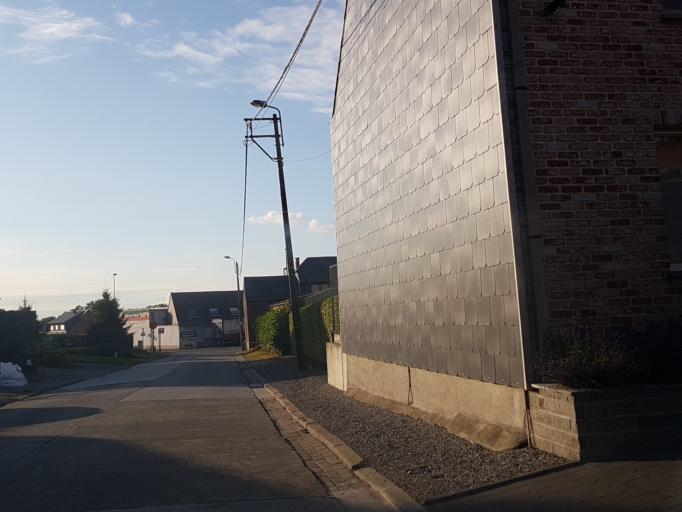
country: BE
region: Flanders
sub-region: Provincie Vlaams-Brabant
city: Opwijk
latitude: 50.9504
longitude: 4.1367
